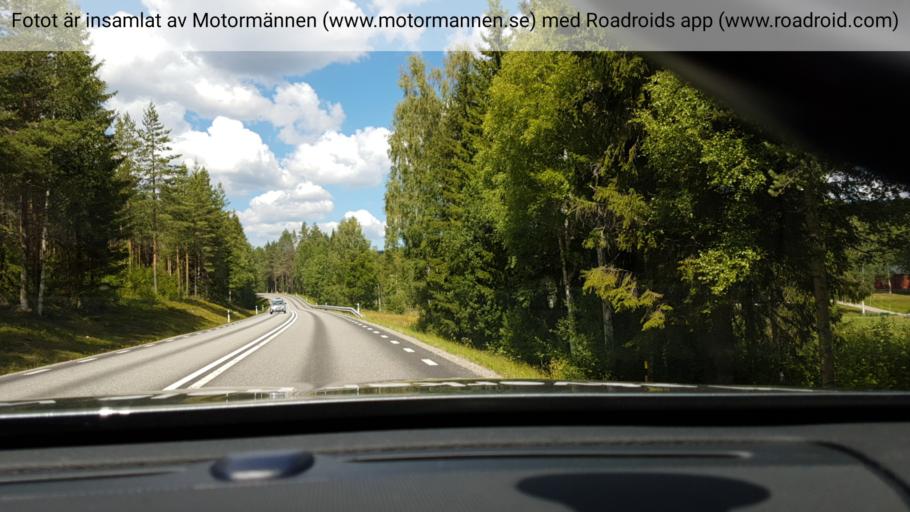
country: SE
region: Dalarna
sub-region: Faluns Kommun
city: Bjursas
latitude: 60.7376
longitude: 15.4320
